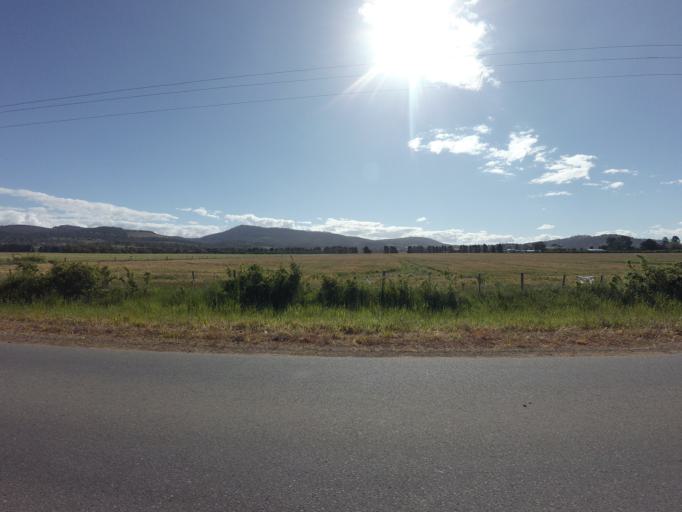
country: AU
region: Tasmania
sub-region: Clarence
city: Cambridge
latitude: -42.7581
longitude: 147.4163
